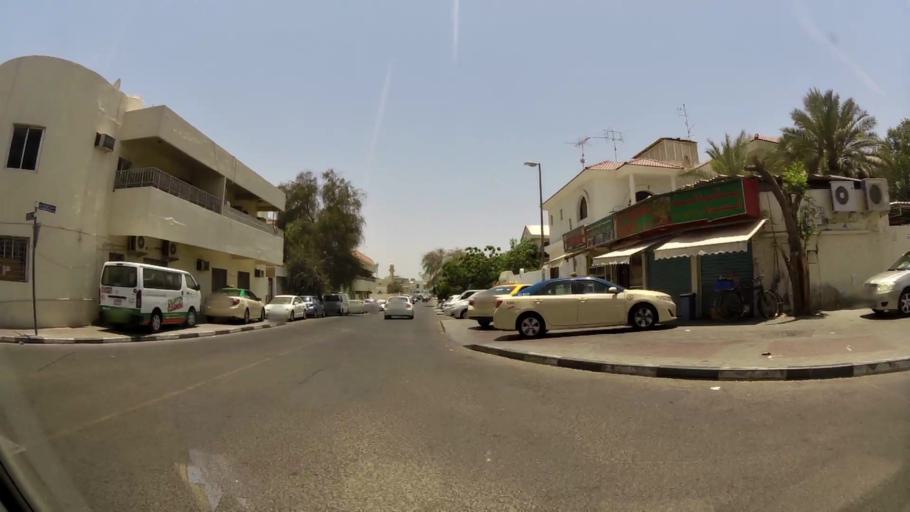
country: AE
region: Ash Shariqah
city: Sharjah
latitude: 25.2867
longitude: 55.3300
